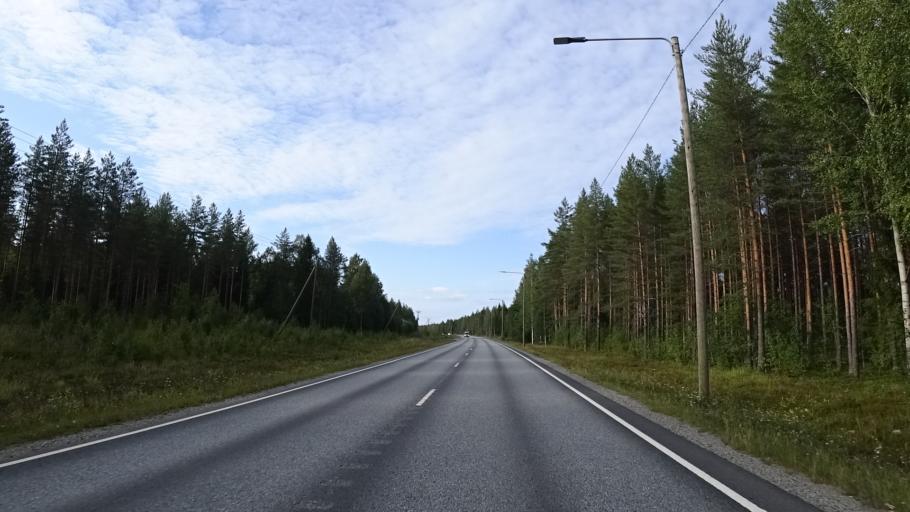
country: FI
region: North Karelia
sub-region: Joensuu
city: Eno
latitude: 62.8706
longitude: 30.2020
